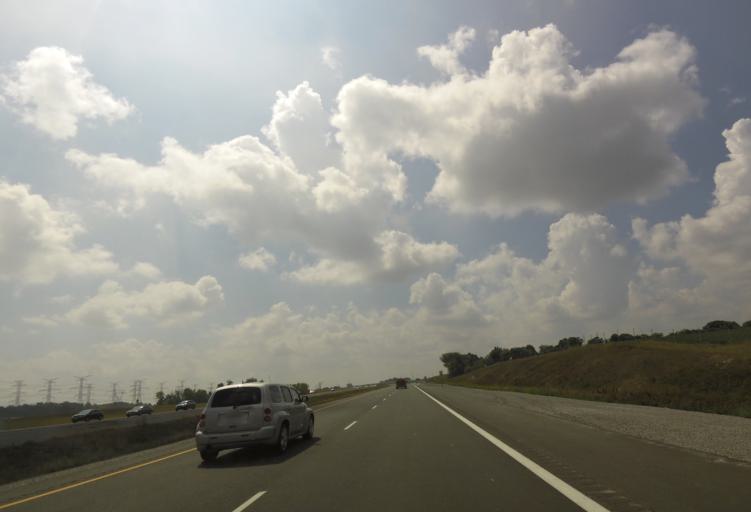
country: CA
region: Ontario
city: Oshawa
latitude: 43.9759
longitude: -78.8928
